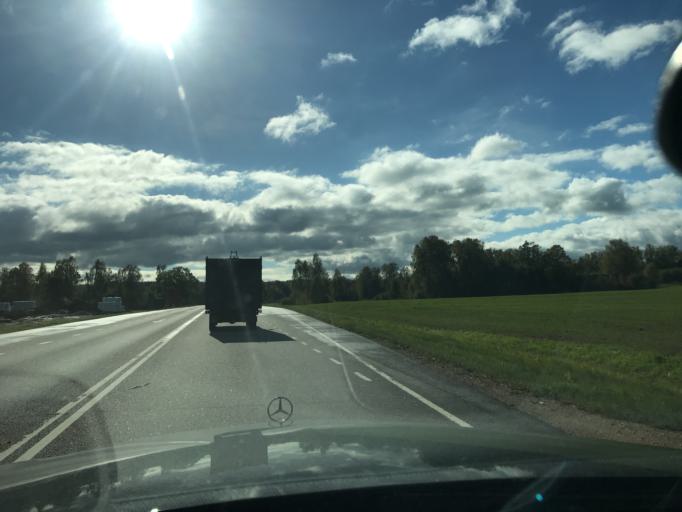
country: EE
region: Vorumaa
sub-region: Voru linn
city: Voru
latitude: 57.8152
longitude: 27.0648
